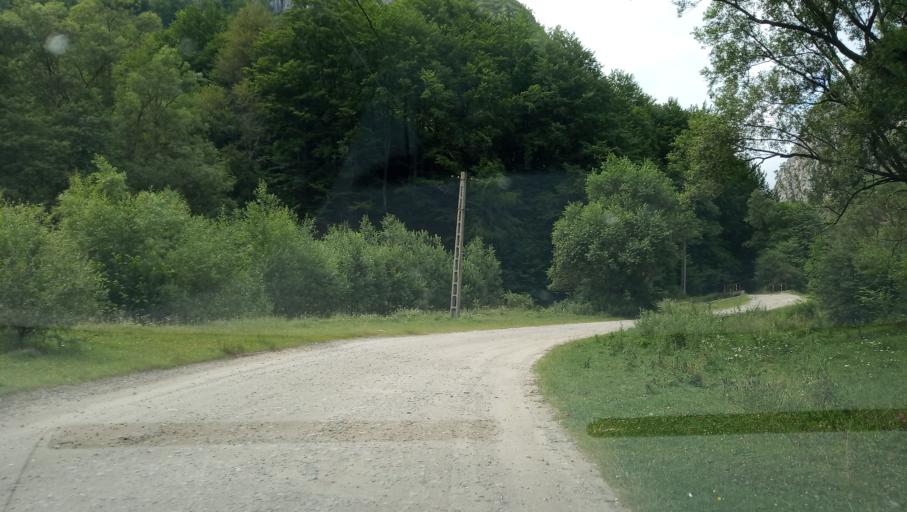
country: RO
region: Hunedoara
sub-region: Oras Petrila
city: Petrila
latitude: 45.4700
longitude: 23.4182
